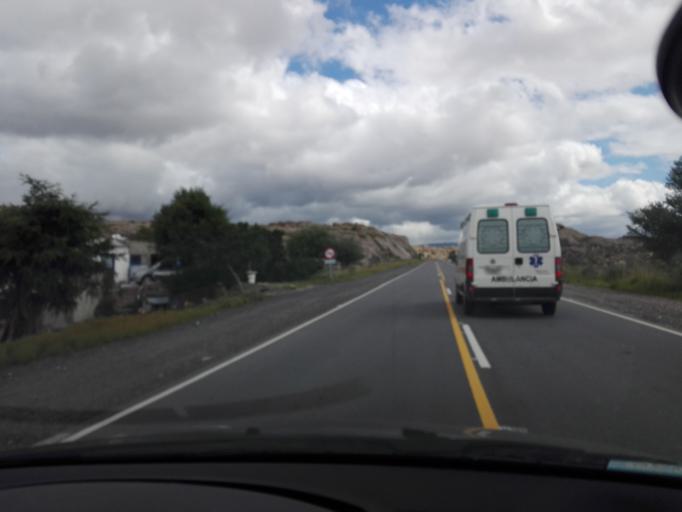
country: AR
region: Cordoba
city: Mina Clavero
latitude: -31.7269
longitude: -64.9012
